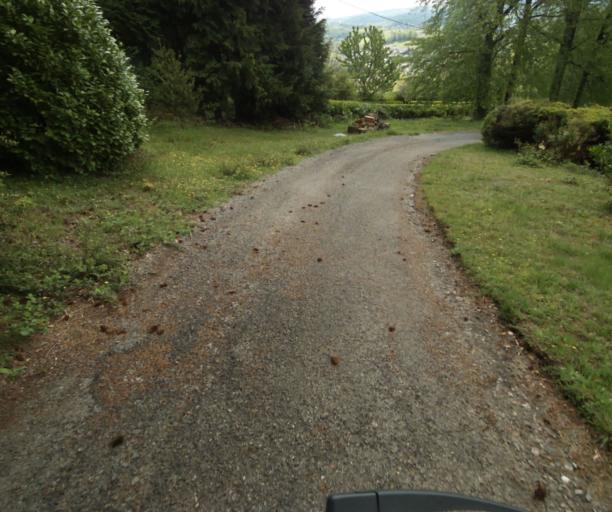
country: FR
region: Limousin
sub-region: Departement de la Correze
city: Naves
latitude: 45.2929
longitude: 1.7680
